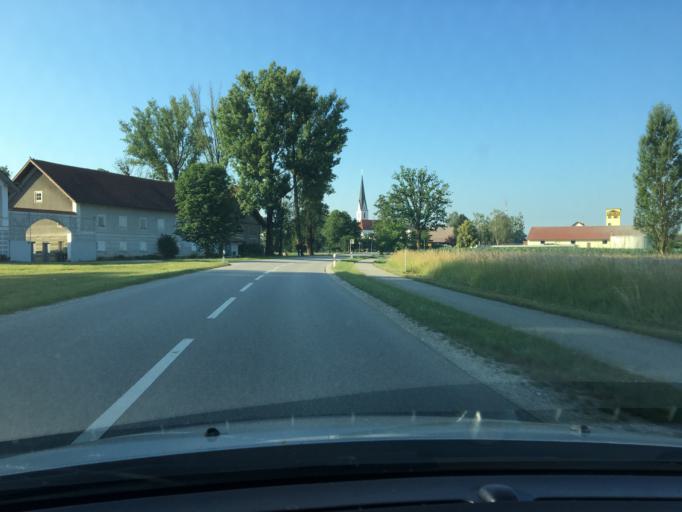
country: DE
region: Bavaria
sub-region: Lower Bavaria
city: Vilsbiburg
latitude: 48.4339
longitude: 12.3437
